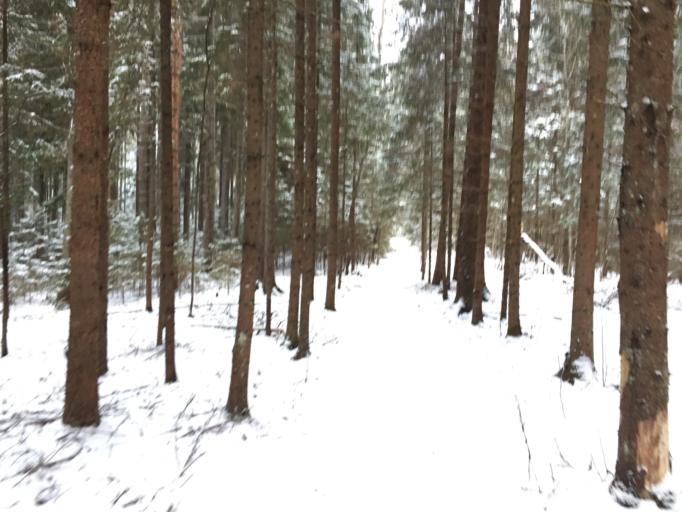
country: LV
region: Ligatne
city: Ligatne
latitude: 57.2401
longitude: 25.0516
